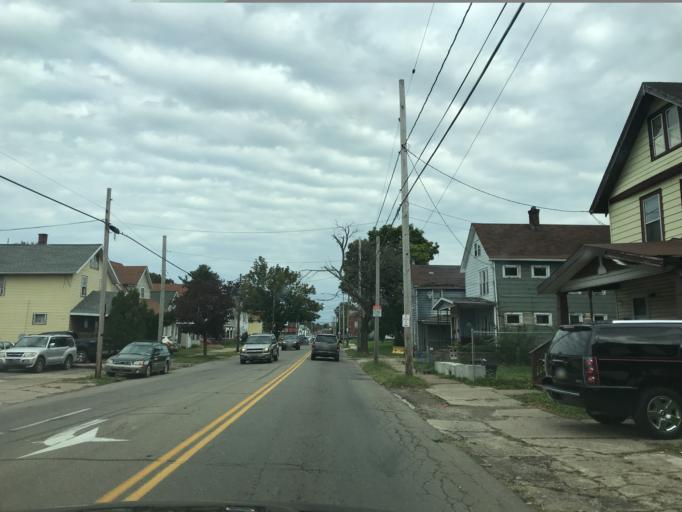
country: US
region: Pennsylvania
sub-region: Erie County
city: Erie
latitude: 42.1200
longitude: -80.0513
